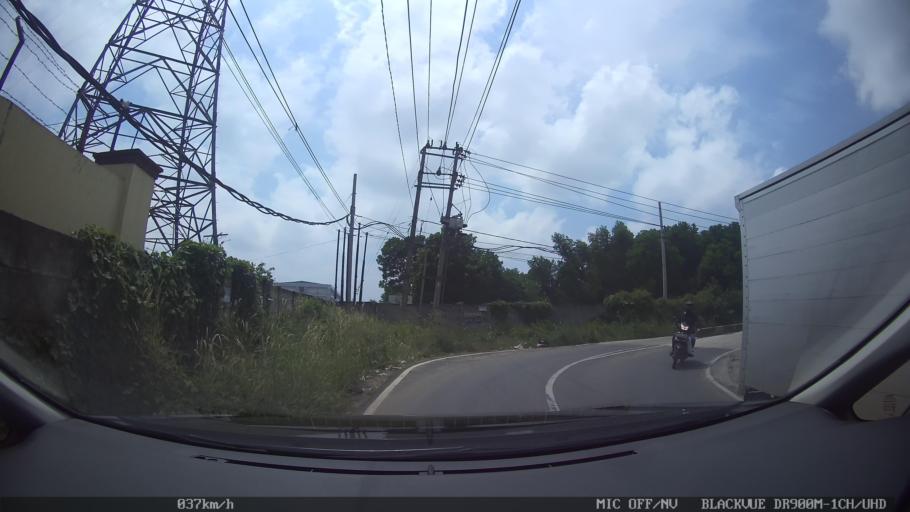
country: ID
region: Lampung
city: Kedaton
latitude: -5.3613
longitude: 105.3081
